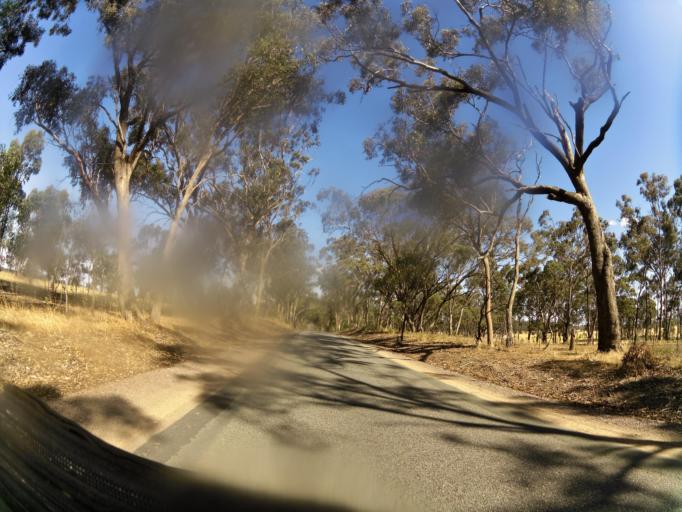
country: AU
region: Victoria
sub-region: Campaspe
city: Kyabram
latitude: -36.8786
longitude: 145.0879
